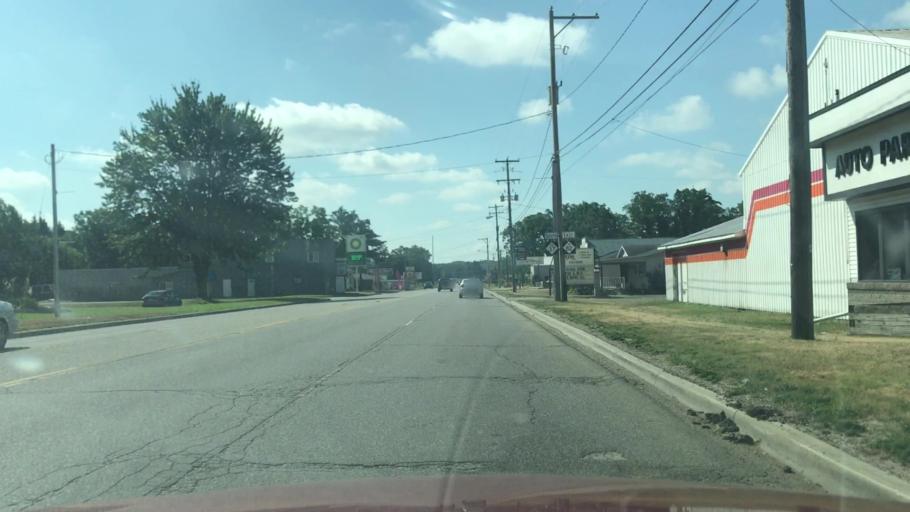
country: US
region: Michigan
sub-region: Newaygo County
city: Newaygo
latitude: 43.4101
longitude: -85.8058
